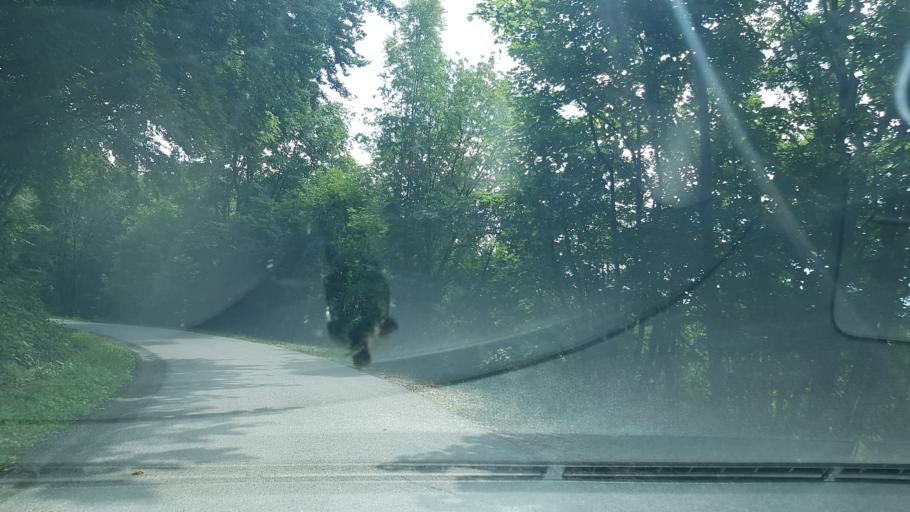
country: SI
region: Kanal
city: Deskle
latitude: 46.0773
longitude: 13.5860
